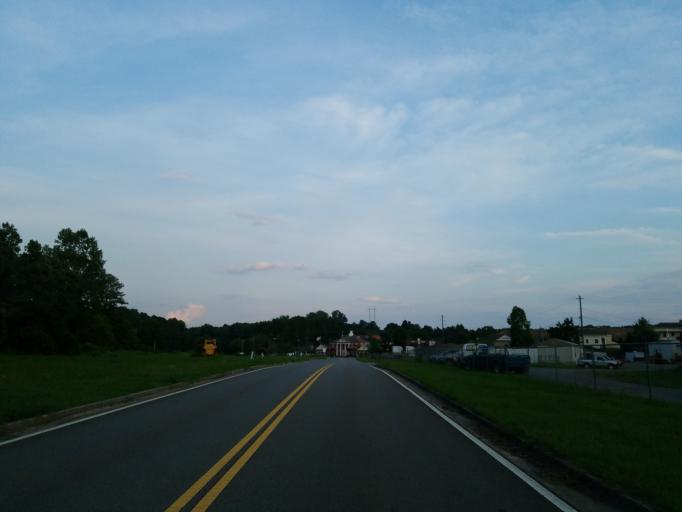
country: US
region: Georgia
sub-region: Pickens County
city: Jasper
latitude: 34.4676
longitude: -84.4516
